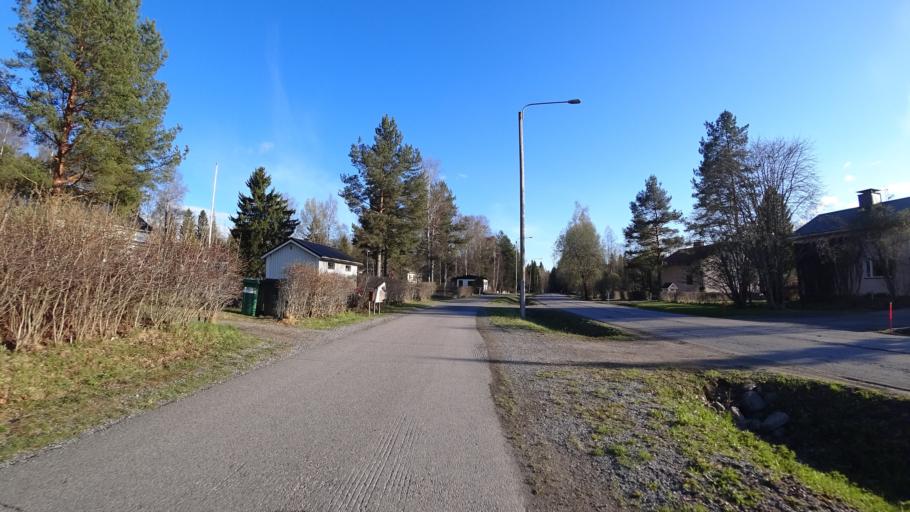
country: FI
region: Pirkanmaa
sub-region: Tampere
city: Yloejaervi
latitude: 61.5064
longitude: 23.5936
